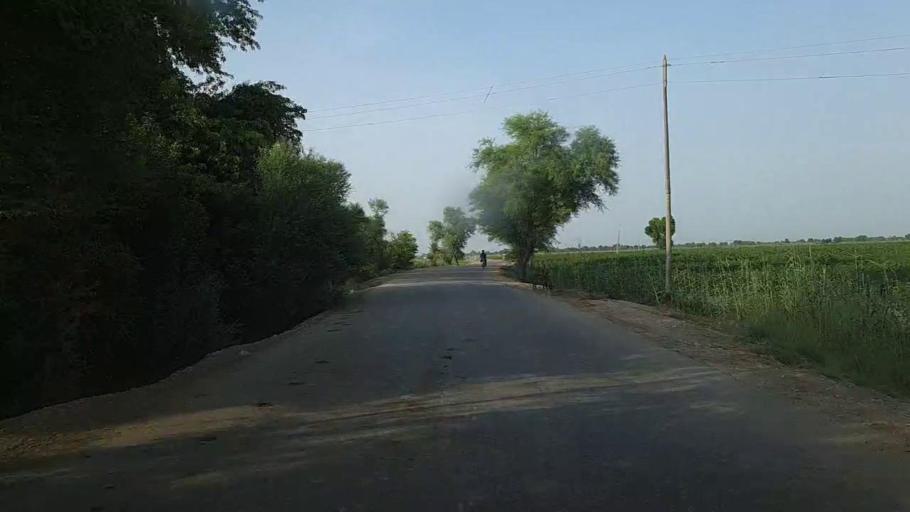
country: PK
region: Sindh
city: Khairpur
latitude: 28.0874
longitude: 69.8016
